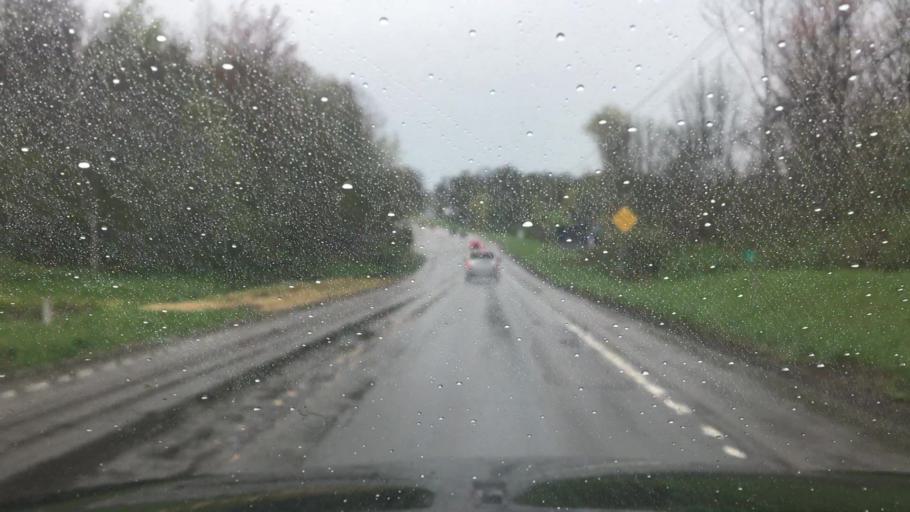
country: US
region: New York
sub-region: Chautauqua County
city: Lakewood
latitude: 42.1434
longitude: -79.4020
